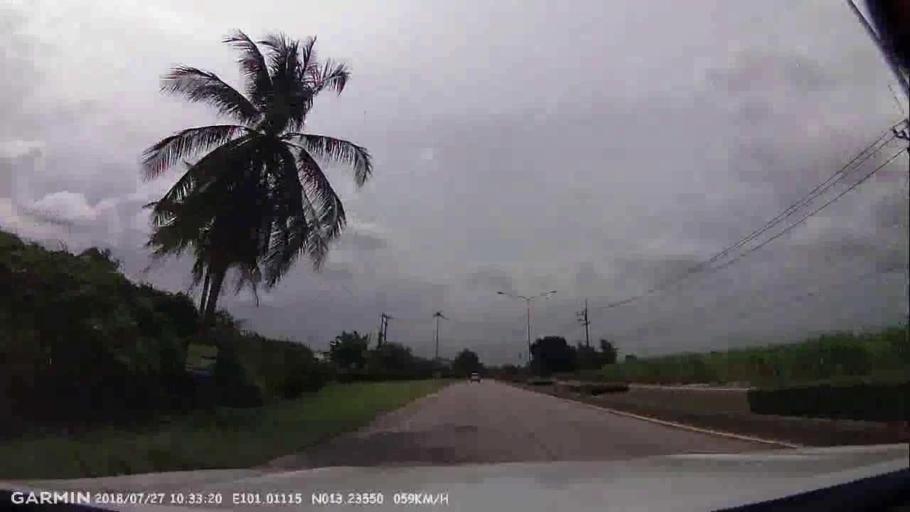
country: TH
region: Chon Buri
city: Si Racha
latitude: 13.2354
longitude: 101.0113
